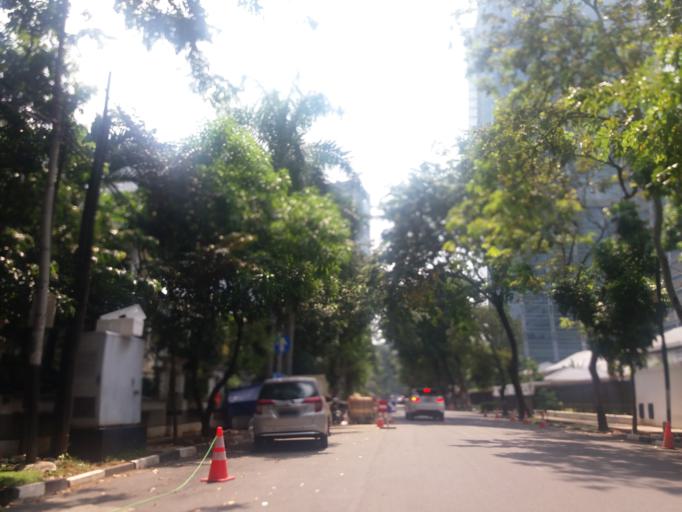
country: ID
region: Jakarta Raya
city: Jakarta
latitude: -6.2283
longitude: 106.8319
